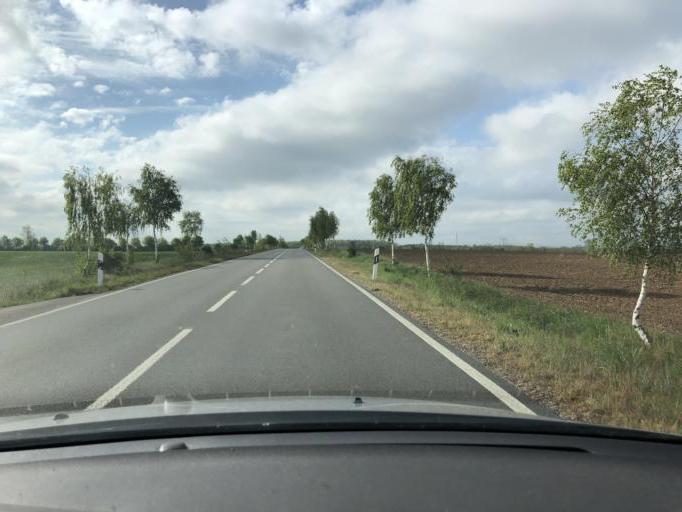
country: DE
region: Saxony
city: Neukieritzsch
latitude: 51.1624
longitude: 12.4191
